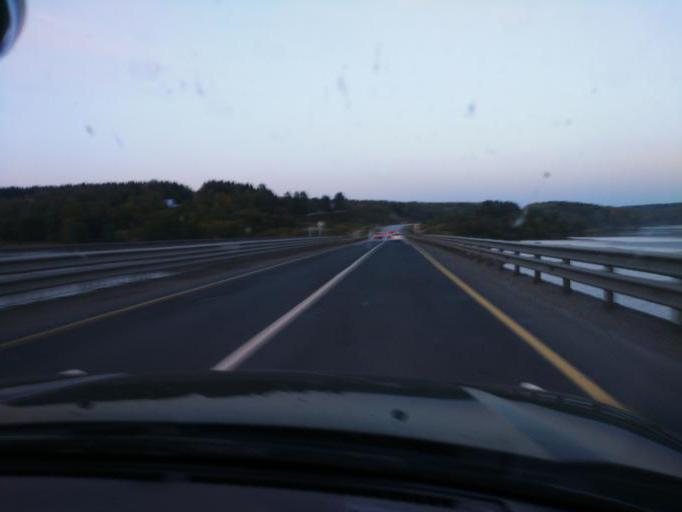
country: RU
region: Perm
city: Sylva
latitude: 58.2961
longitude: 56.8526
